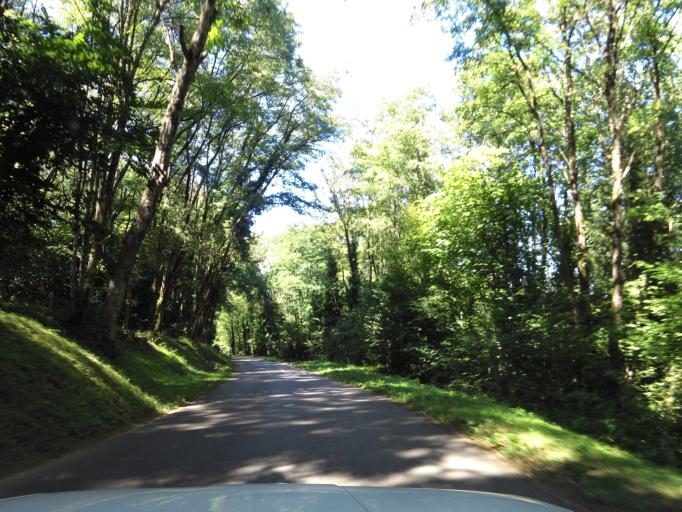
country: FR
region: Rhone-Alpes
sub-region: Departement de l'Ain
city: Vaux-en-Bugey
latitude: 45.9384
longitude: 5.3638
